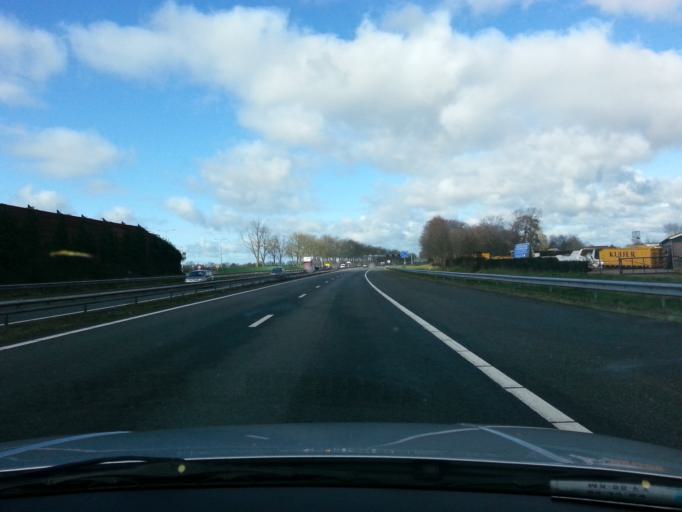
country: NL
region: Gelderland
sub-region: Gemeente Nijkerk
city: Nijkerk
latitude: 52.2008
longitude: 5.4391
